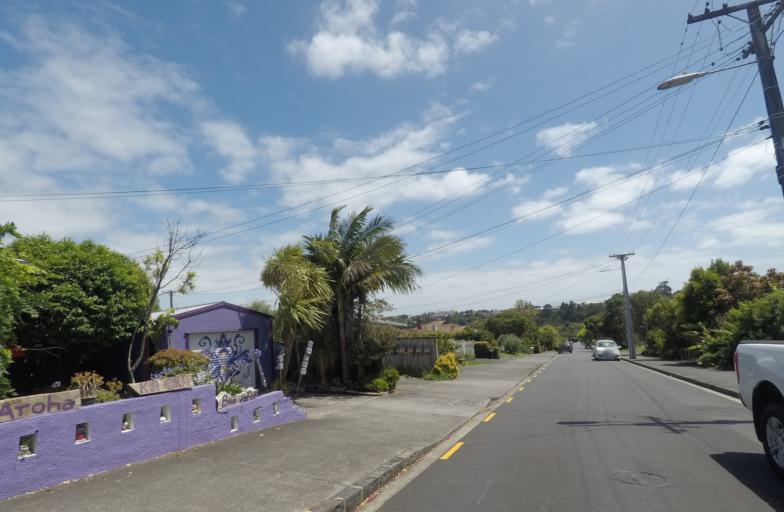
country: NZ
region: Auckland
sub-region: Auckland
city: Auckland
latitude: -36.8723
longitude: 174.7377
